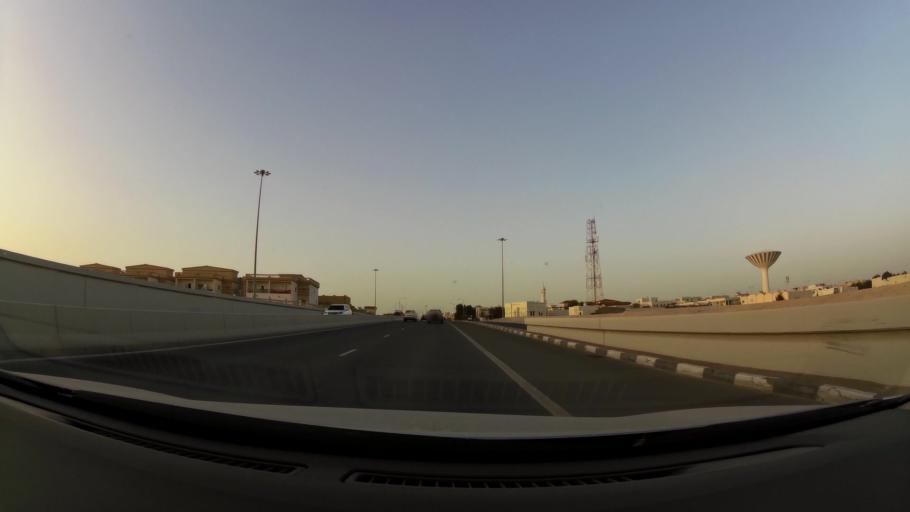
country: QA
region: Baladiyat ar Rayyan
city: Ar Rayyan
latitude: 25.3224
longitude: 51.4606
